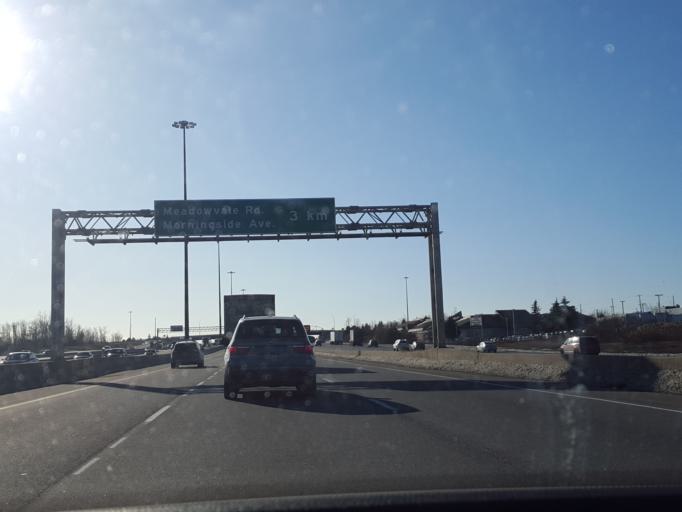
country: CA
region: Ontario
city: Ajax
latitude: 43.8210
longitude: -79.1084
